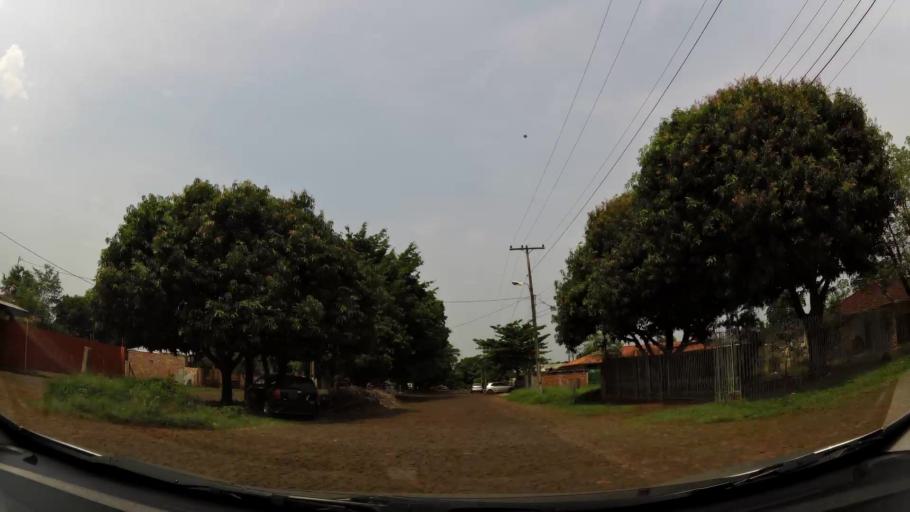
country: PY
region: Alto Parana
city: Presidente Franco
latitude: -25.5458
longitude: -54.6287
